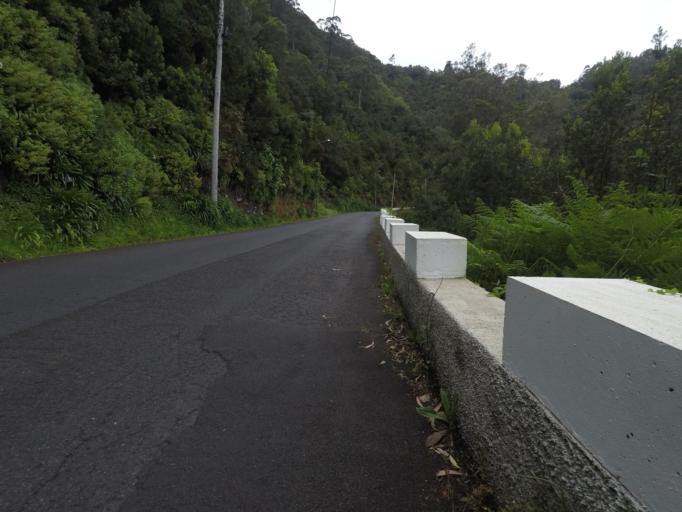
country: PT
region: Madeira
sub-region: Santana
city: Santana
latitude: 32.7906
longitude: -16.8611
